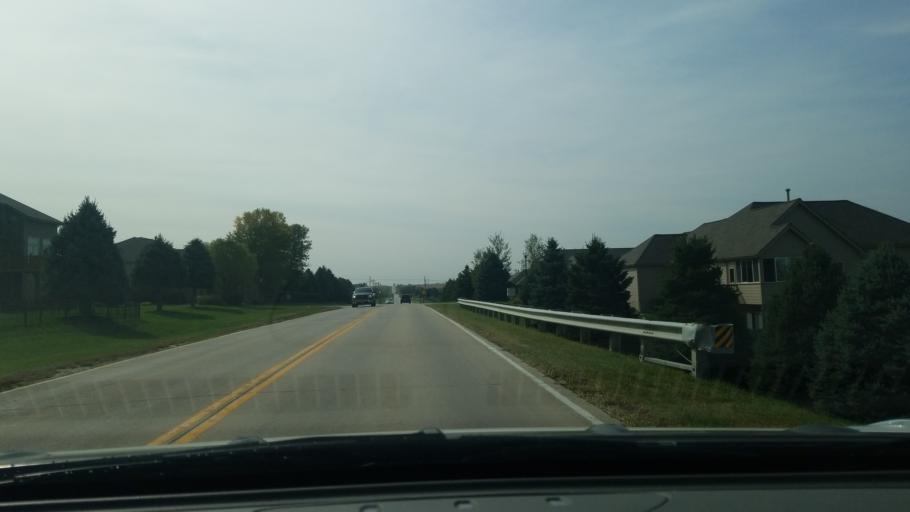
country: US
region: Nebraska
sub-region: Sarpy County
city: Papillion
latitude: 41.1357
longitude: -96.0621
